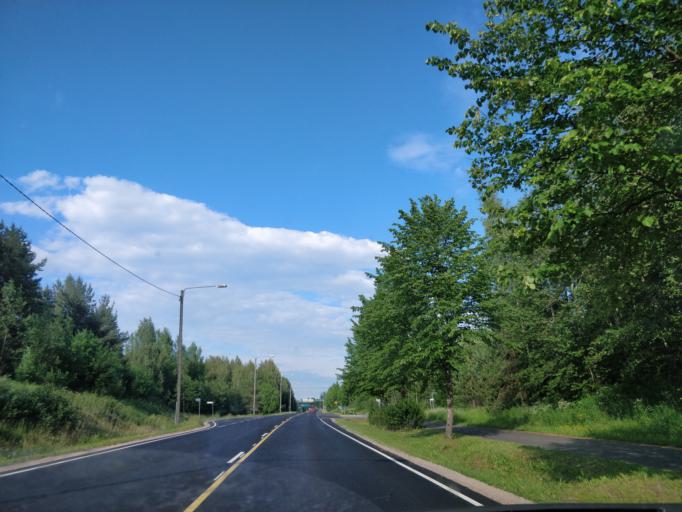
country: FI
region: Haeme
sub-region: Haemeenlinna
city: Tervakoski
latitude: 60.8221
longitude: 24.6575
